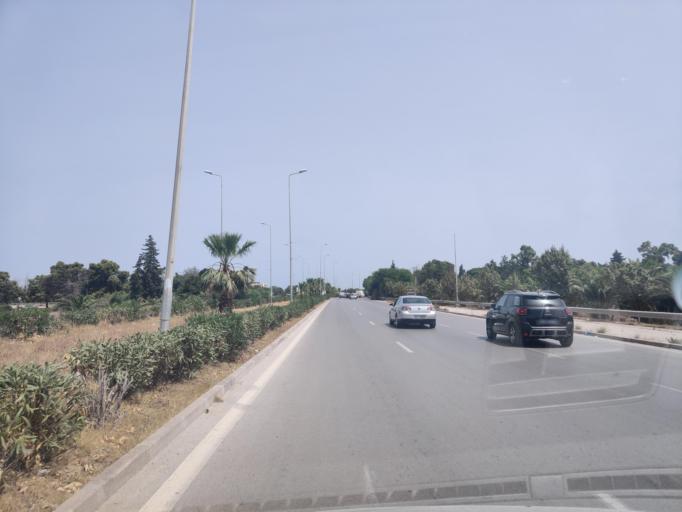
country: TN
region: Tunis
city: Carthage
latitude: 36.8572
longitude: 10.3114
